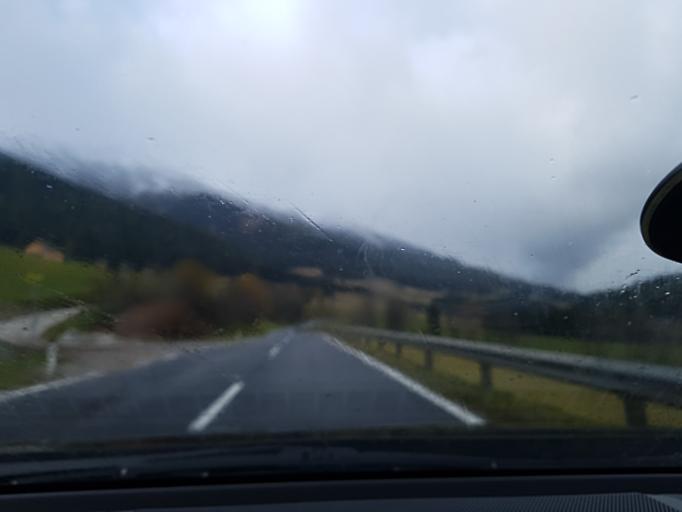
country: AT
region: Styria
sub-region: Politischer Bezirk Murtal
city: Sankt Johann am Tauern
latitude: 47.3649
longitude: 14.4652
